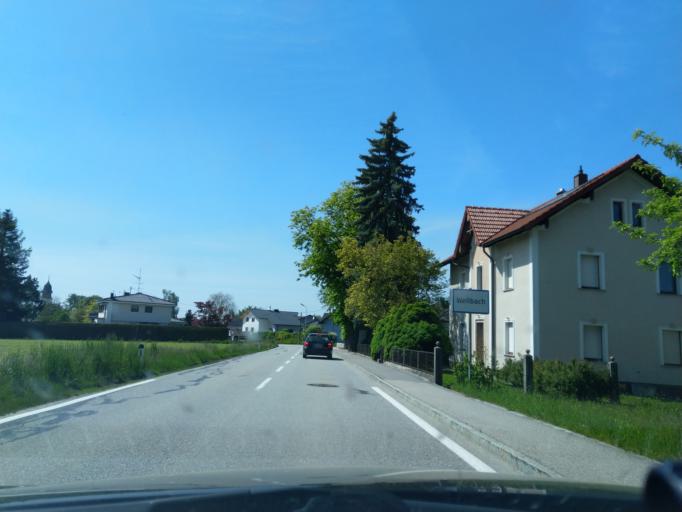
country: DE
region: Bavaria
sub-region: Lower Bavaria
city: Bad Fussing
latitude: 48.2770
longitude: 13.3773
